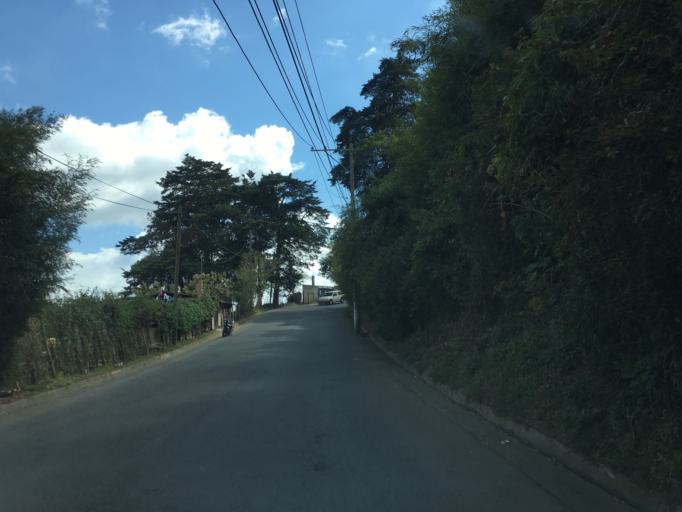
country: GT
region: Guatemala
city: San Jose Pinula
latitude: 14.5597
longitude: -90.4418
